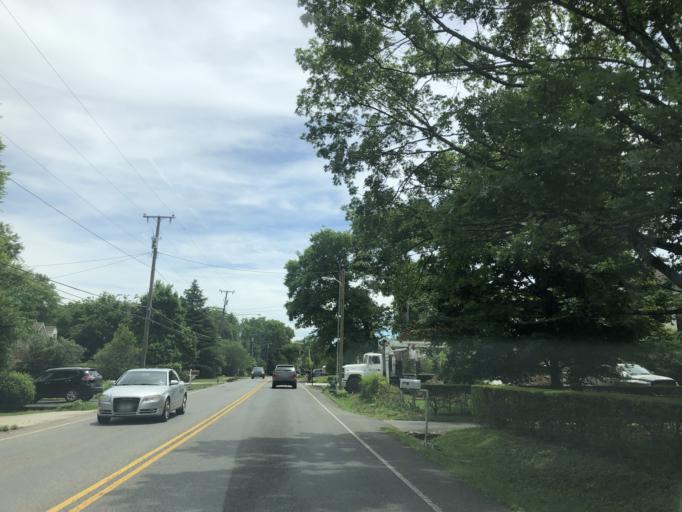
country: US
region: Tennessee
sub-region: Davidson County
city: Oak Hill
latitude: 36.1129
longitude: -86.7979
